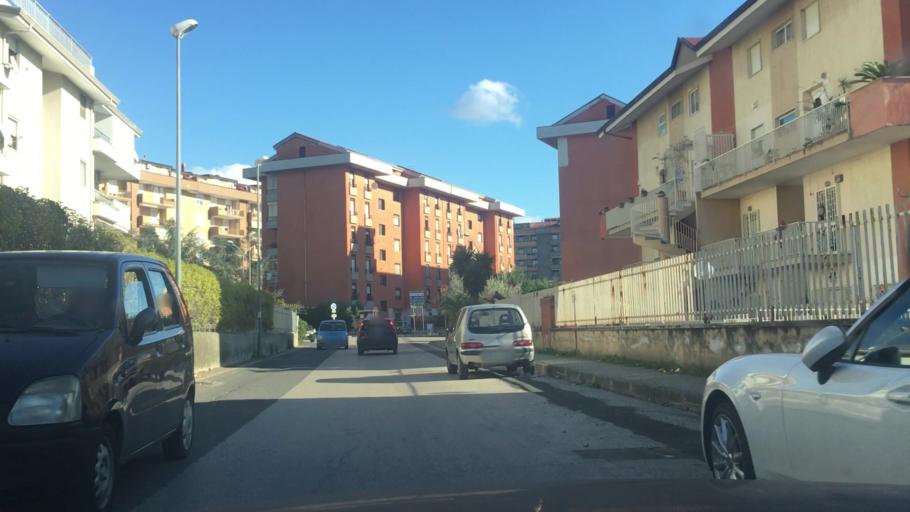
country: IT
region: Campania
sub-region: Provincia di Caserta
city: Caserta
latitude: 41.0701
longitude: 14.3524
